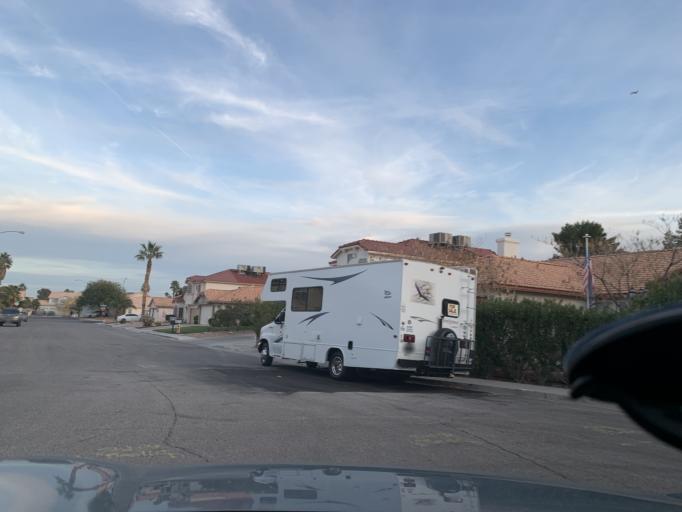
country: US
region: Nevada
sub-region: Clark County
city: Spring Valley
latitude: 36.0914
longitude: -115.2354
